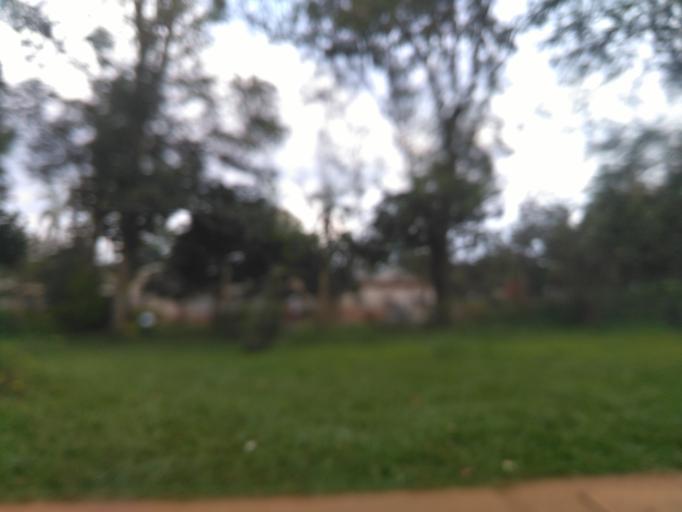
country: UG
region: Eastern Region
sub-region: Jinja District
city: Jinja
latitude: 0.4376
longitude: 33.2014
